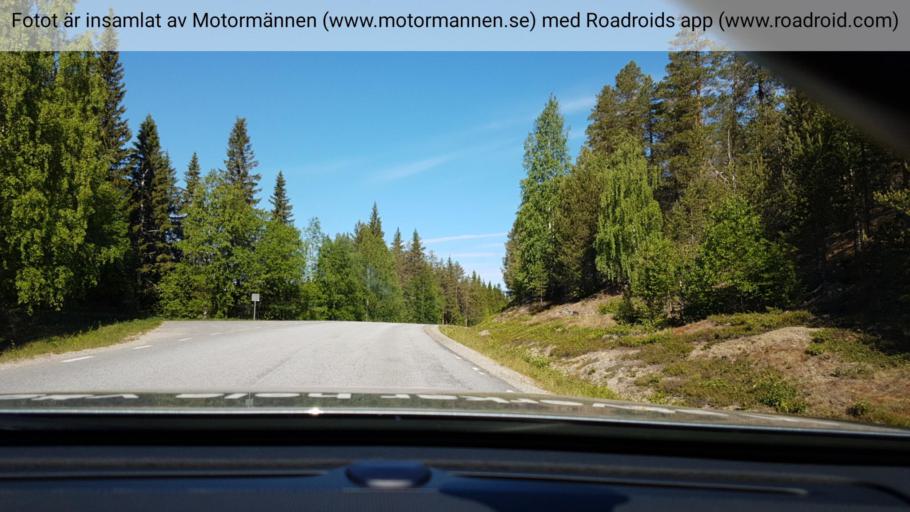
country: SE
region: Vaesterbotten
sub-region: Bjurholms Kommun
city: Bjurholm
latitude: 64.0011
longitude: 18.7366
